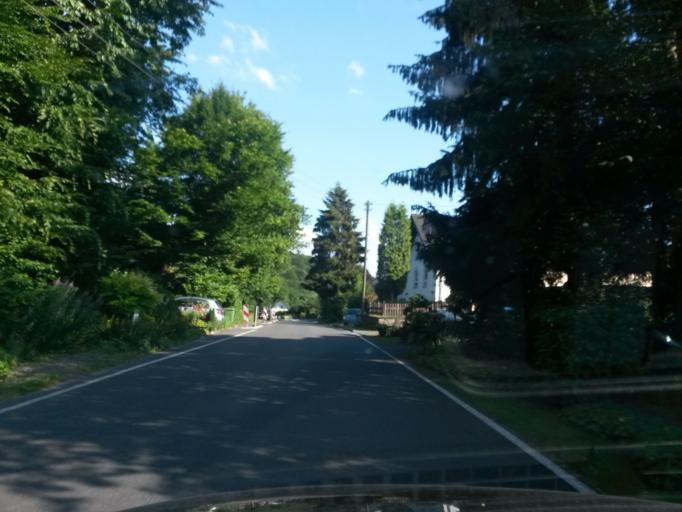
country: DE
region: North Rhine-Westphalia
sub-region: Regierungsbezirk Koln
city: Much
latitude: 50.9264
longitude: 7.4055
